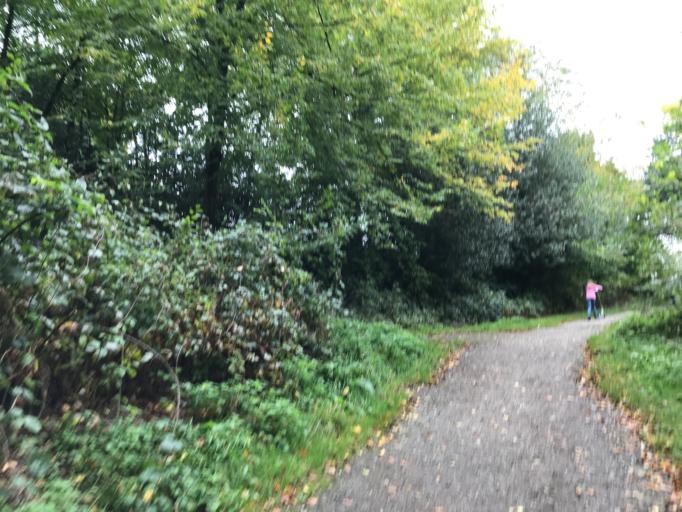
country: DE
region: North Rhine-Westphalia
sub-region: Regierungsbezirk Dusseldorf
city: Essen
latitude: 51.4108
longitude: 7.0290
